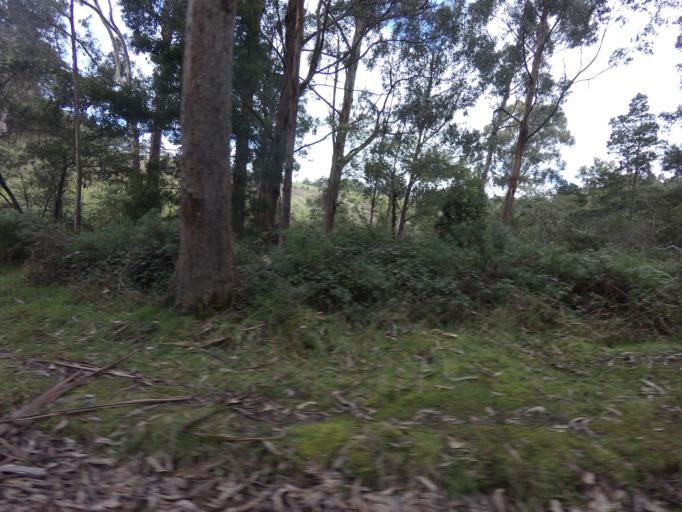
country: AU
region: Tasmania
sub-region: Huon Valley
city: Cygnet
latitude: -43.4076
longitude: 147.0174
